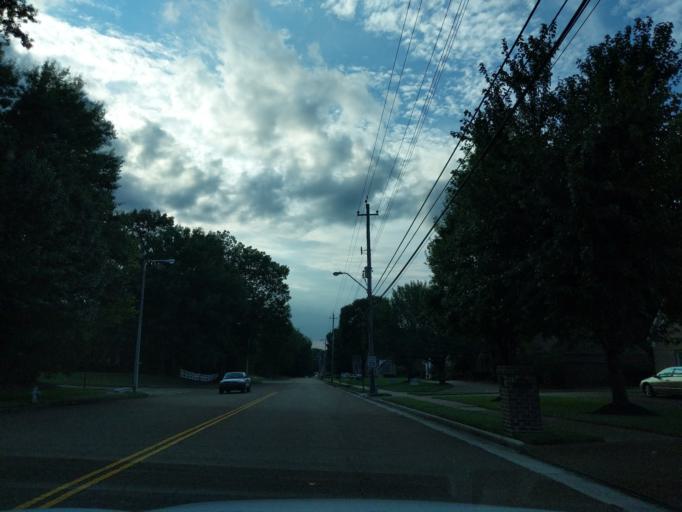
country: US
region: Tennessee
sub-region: Shelby County
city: Germantown
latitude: 35.0669
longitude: -89.7706
